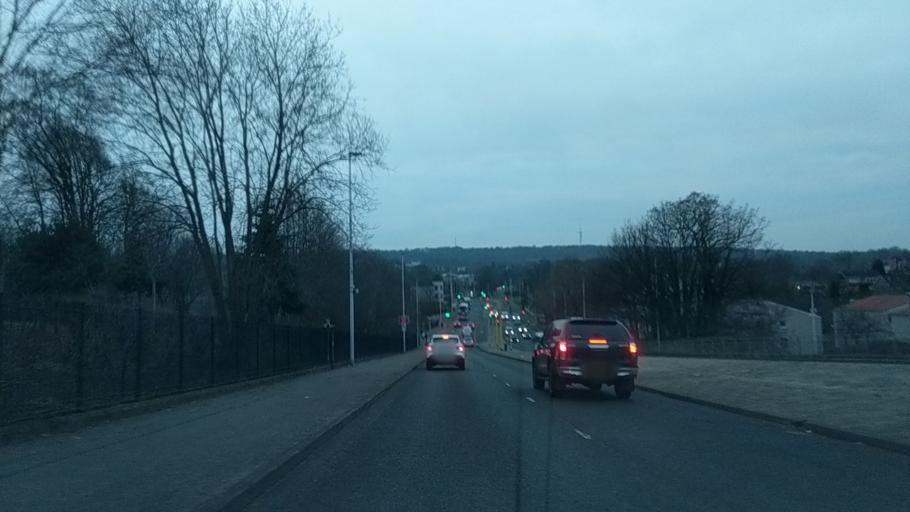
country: GB
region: Scotland
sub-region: South Lanarkshire
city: Rutherglen
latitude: 55.8223
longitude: -4.2161
